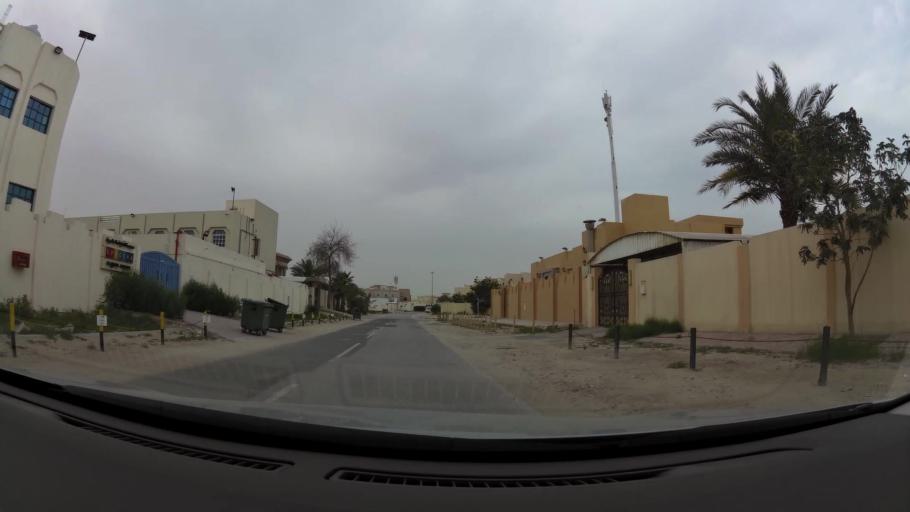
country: QA
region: Baladiyat ar Rayyan
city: Ar Rayyan
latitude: 25.3468
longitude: 51.4756
